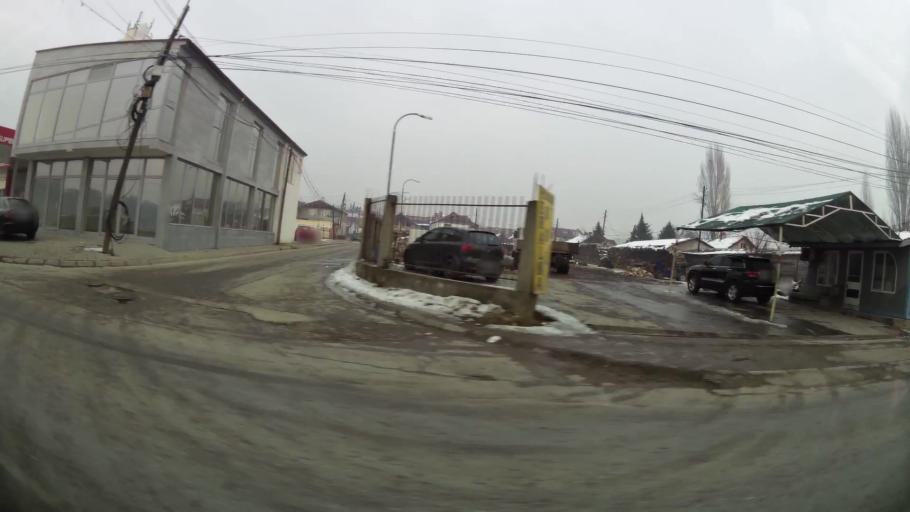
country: MK
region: Suto Orizari
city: Suto Orizare
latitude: 42.0307
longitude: 21.4285
